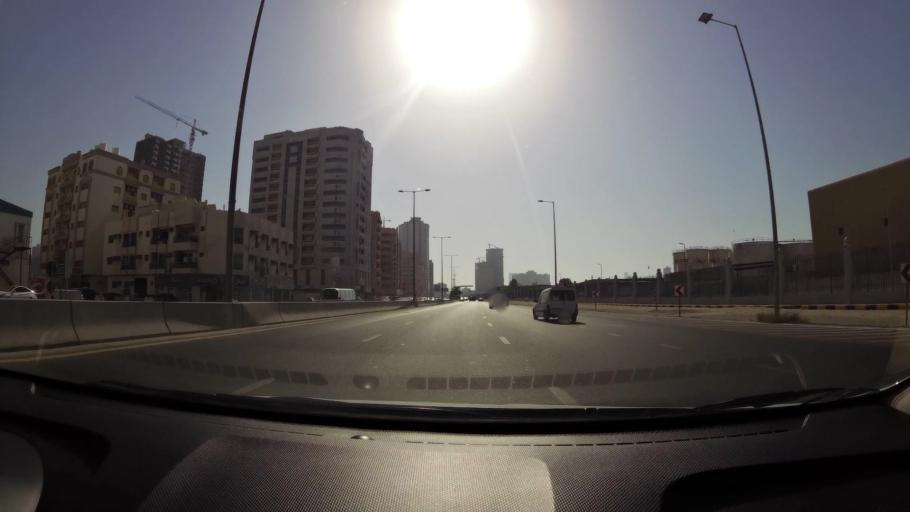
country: AE
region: Ajman
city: Ajman
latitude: 25.3940
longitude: 55.4661
